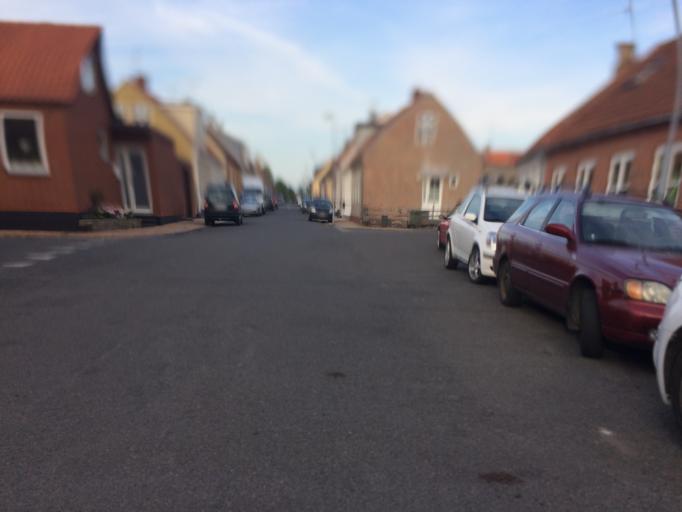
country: DK
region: Capital Region
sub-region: Bornholm Kommune
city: Ronne
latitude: 55.0973
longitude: 14.7040
